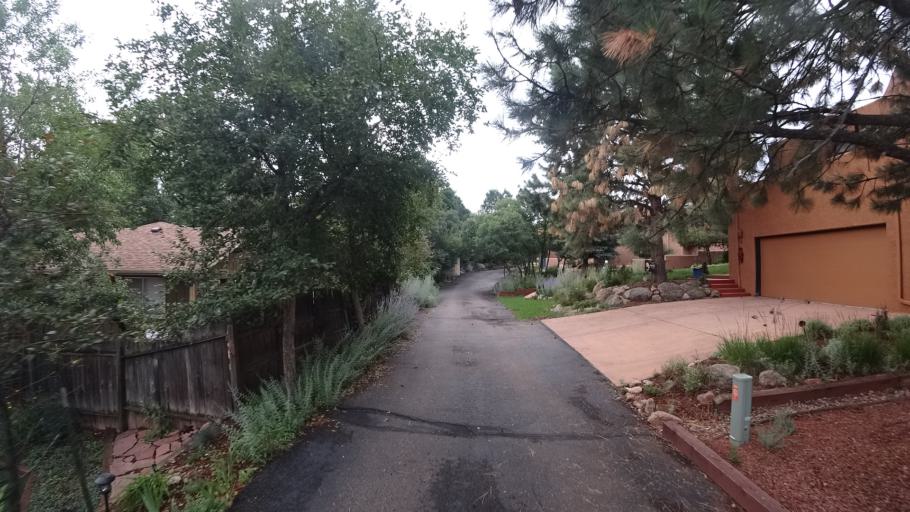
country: US
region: Colorado
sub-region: El Paso County
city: Manitou Springs
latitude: 38.8504
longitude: -104.8967
